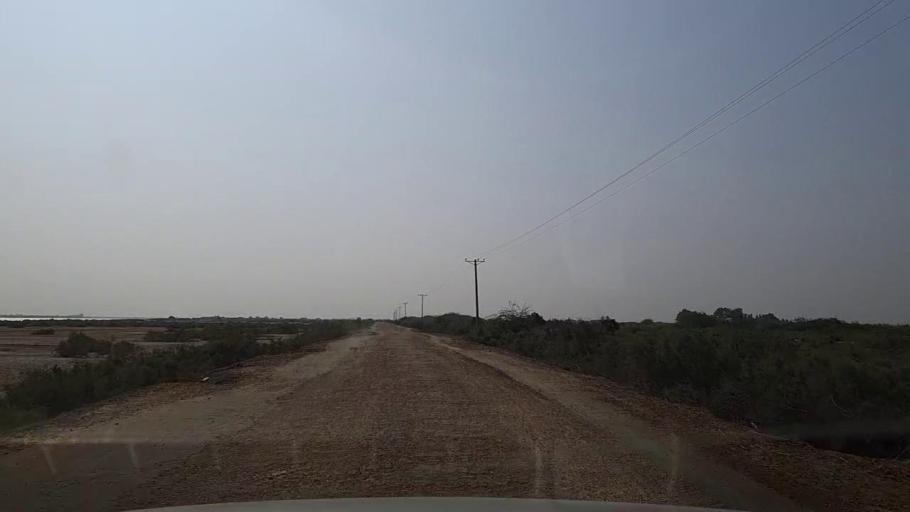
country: PK
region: Sindh
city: Mirpur Sakro
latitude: 24.5381
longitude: 67.5989
